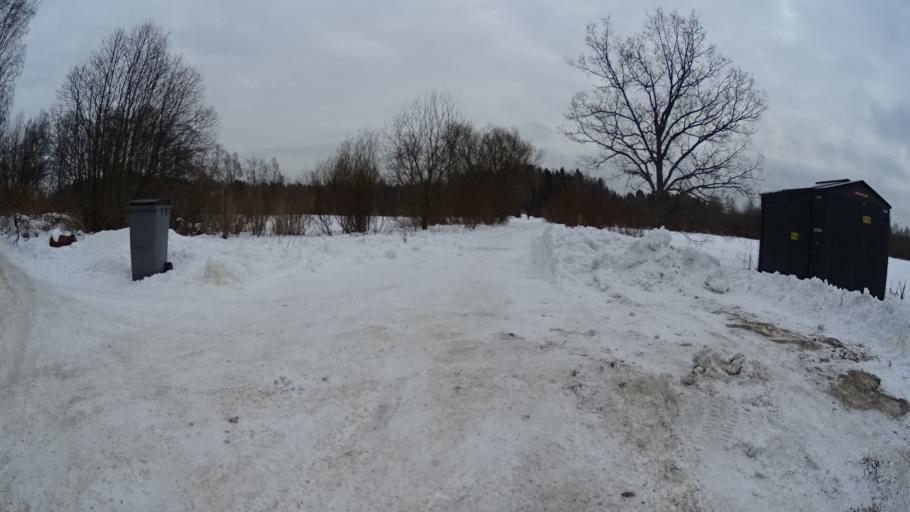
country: FI
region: Uusimaa
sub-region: Helsinki
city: Kauniainen
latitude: 60.2481
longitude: 24.7291
